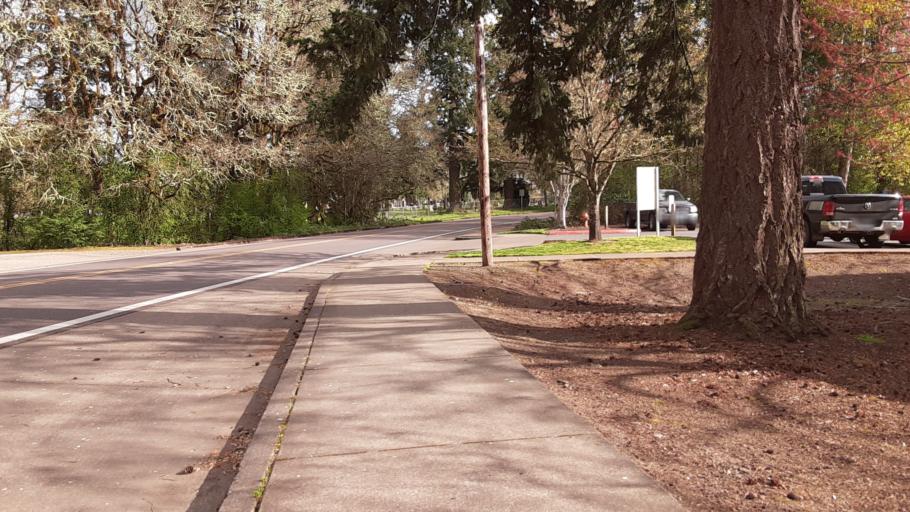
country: US
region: Oregon
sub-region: Benton County
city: Corvallis
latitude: 44.5499
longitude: -123.2562
